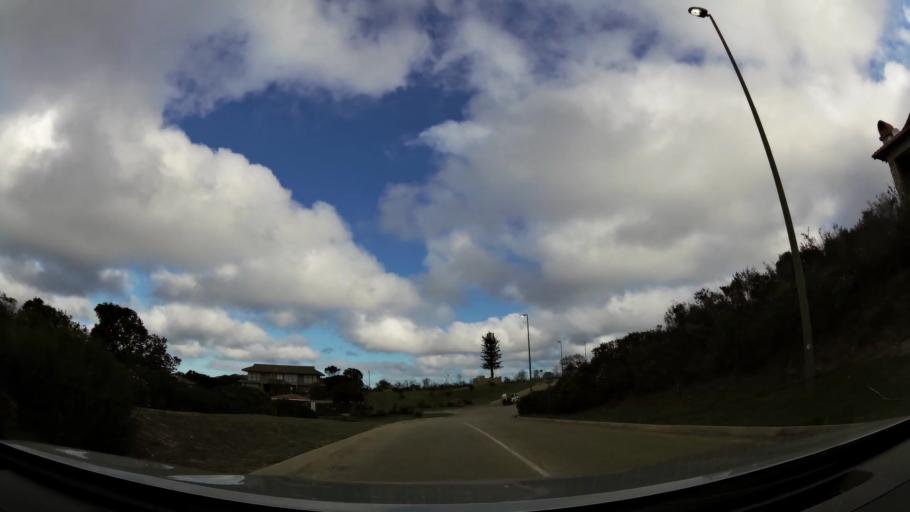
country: ZA
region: Western Cape
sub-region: Eden District Municipality
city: Plettenberg Bay
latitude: -34.0889
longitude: 23.3560
